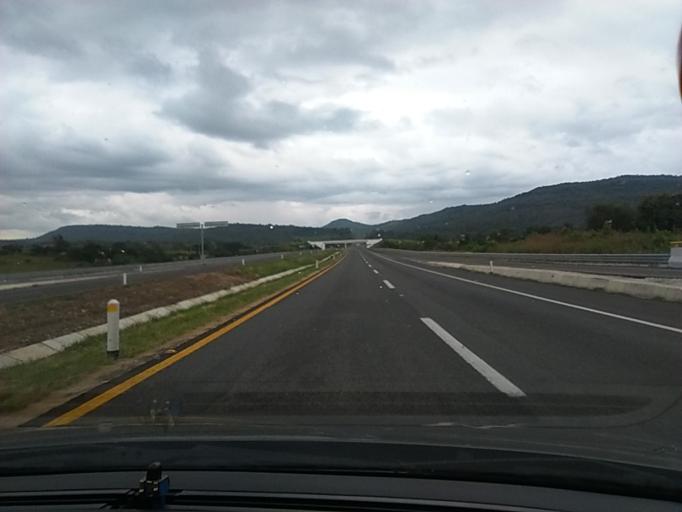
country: MX
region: Jalisco
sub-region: Zapotlanejo
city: La Mezquitera
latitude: 20.5454
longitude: -103.0301
